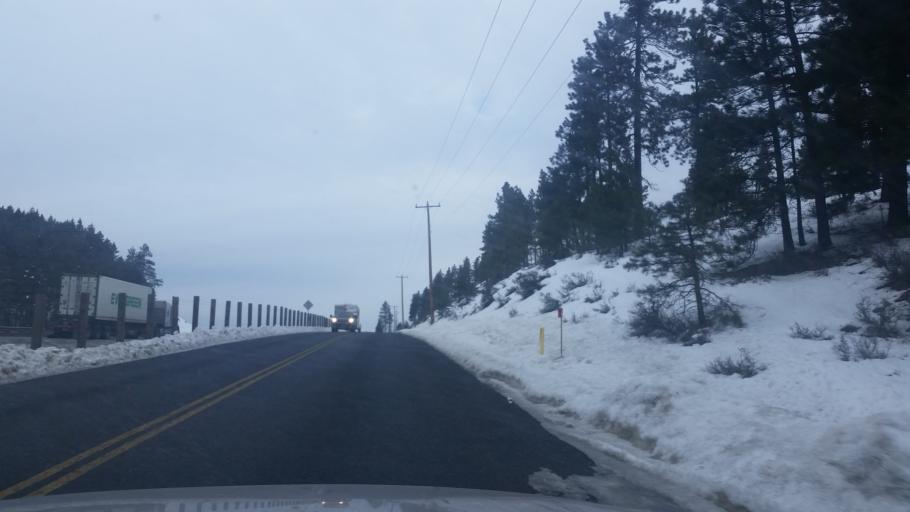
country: US
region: Washington
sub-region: Kittitas County
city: Cle Elum
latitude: 47.1242
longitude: -120.8012
